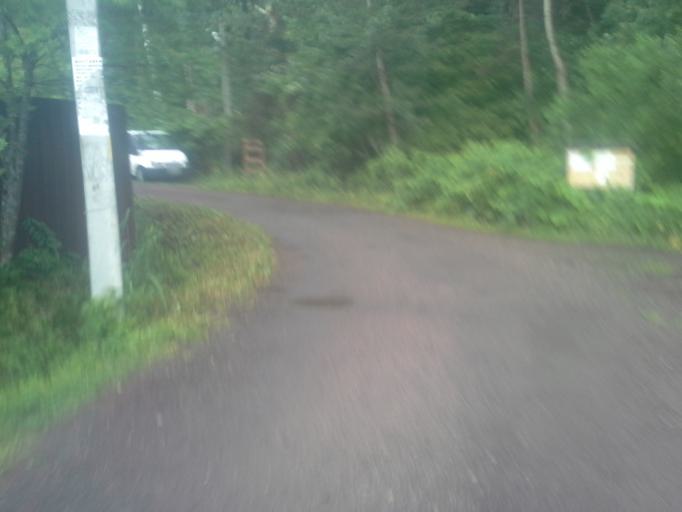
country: RU
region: Moskovskaya
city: Zhavoronki
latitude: 55.6643
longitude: 37.1017
